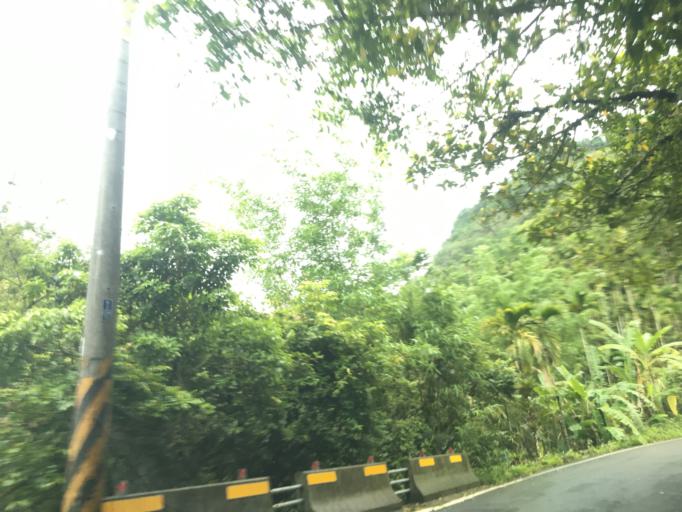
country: TW
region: Taiwan
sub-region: Yunlin
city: Douliu
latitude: 23.5669
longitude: 120.6453
